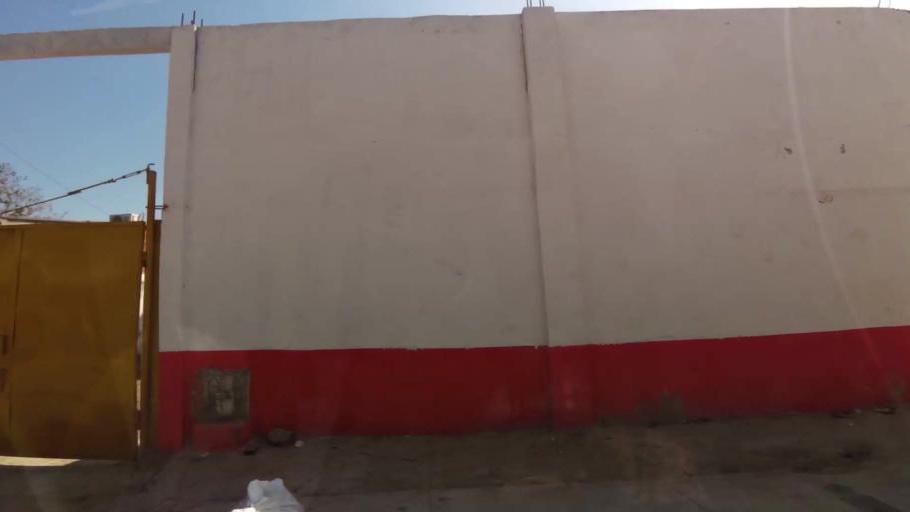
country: CO
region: Bolivar
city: Cartagena
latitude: 10.3707
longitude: -75.4970
